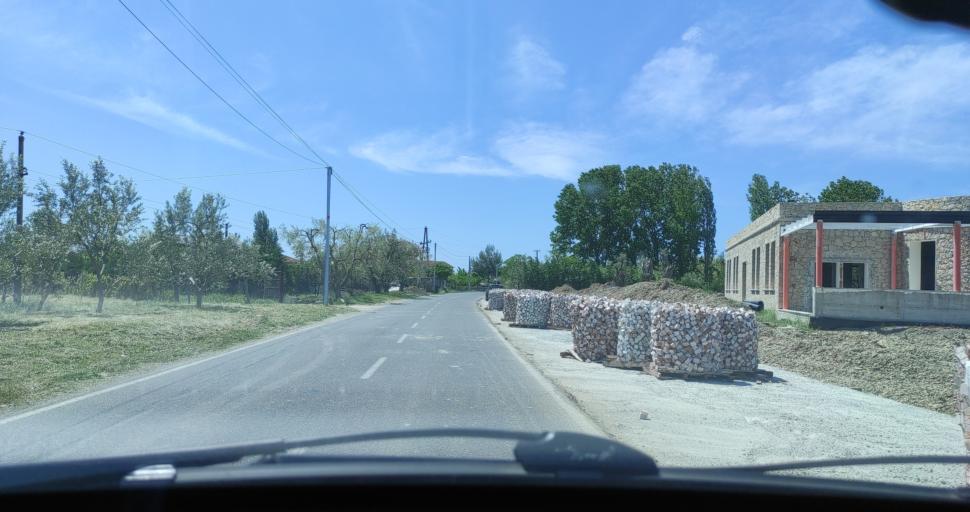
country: AL
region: Lezhe
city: Lezhe
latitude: 41.7606
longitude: 19.6296
